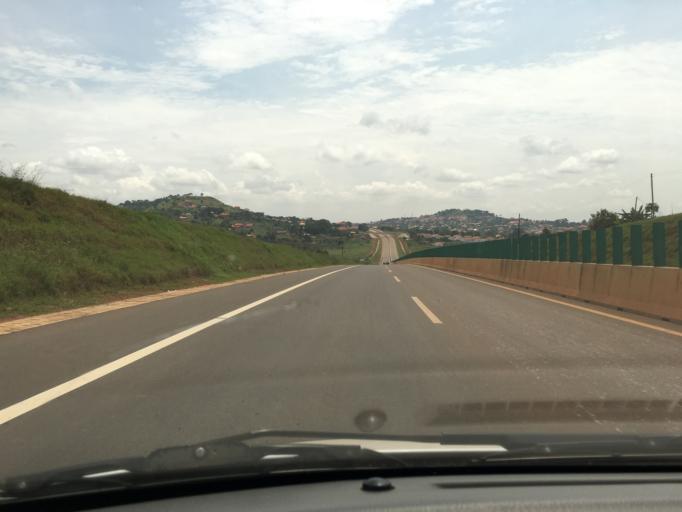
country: UG
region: Central Region
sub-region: Wakiso District
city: Kajansi
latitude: 0.1767
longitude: 32.5176
